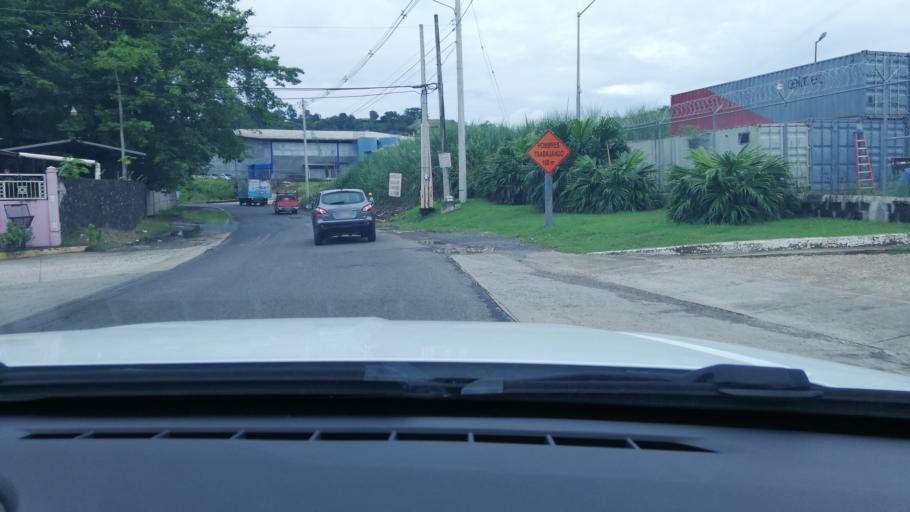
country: PA
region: Panama
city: Las Cumbres
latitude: 9.0737
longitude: -79.5188
